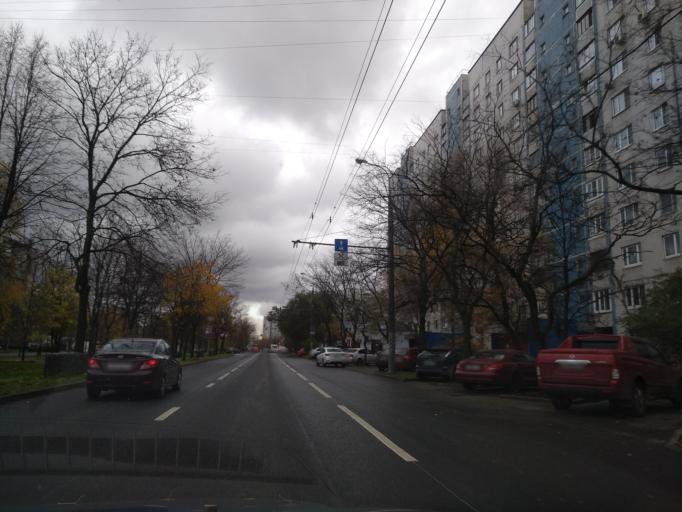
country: RU
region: Moscow
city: Bibirevo
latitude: 55.8928
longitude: 37.6171
